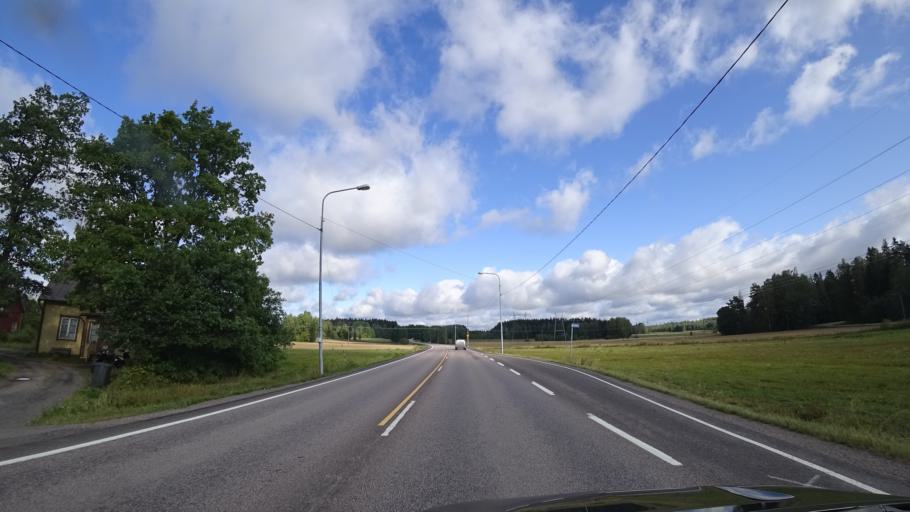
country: FI
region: Uusimaa
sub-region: Helsinki
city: Hyvinge
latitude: 60.5255
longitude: 24.9245
